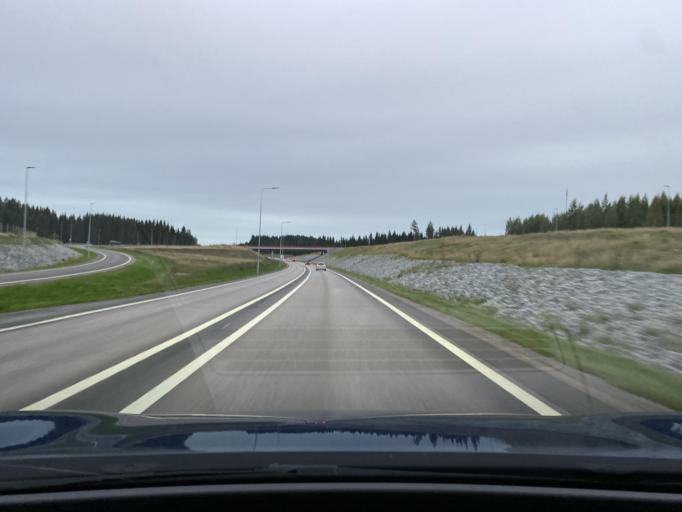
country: FI
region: Paijanne Tavastia
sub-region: Lahti
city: Hollola
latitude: 60.9631
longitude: 25.5246
